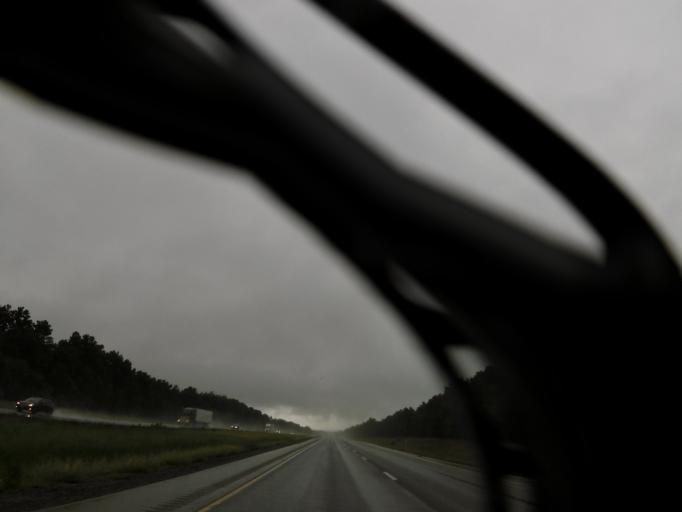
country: US
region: Illinois
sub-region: Williamson County
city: Johnston City
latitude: 37.8569
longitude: -88.9428
